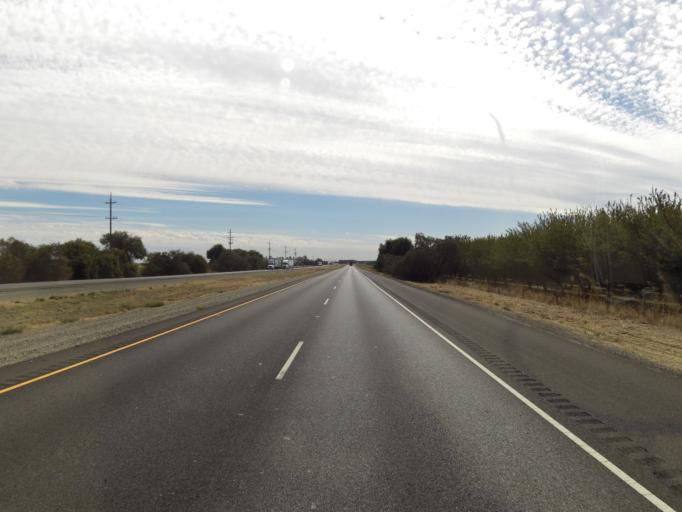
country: US
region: California
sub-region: Colusa County
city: Williams
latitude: 39.1191
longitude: -122.1246
